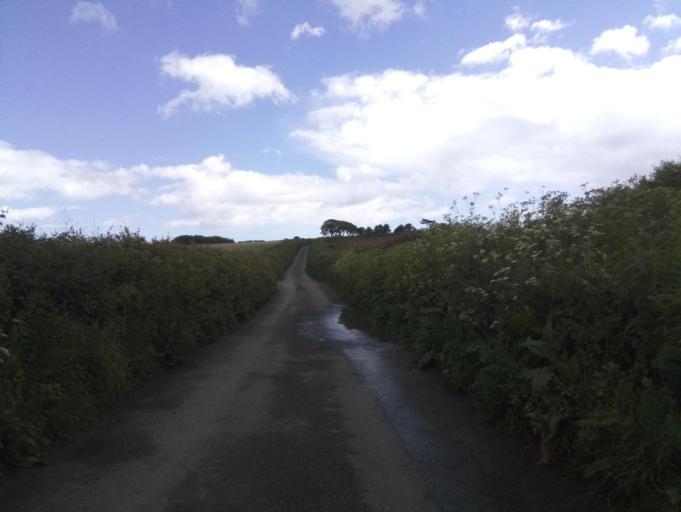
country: GB
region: England
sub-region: Devon
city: Dartmouth
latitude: 50.3536
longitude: -3.5392
